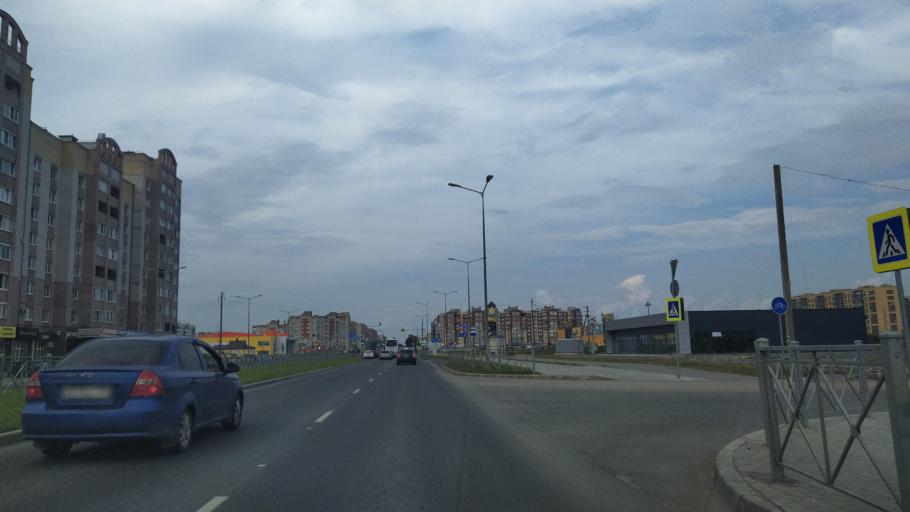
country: RU
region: Novgorod
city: Pankovka
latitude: 58.5042
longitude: 31.2257
